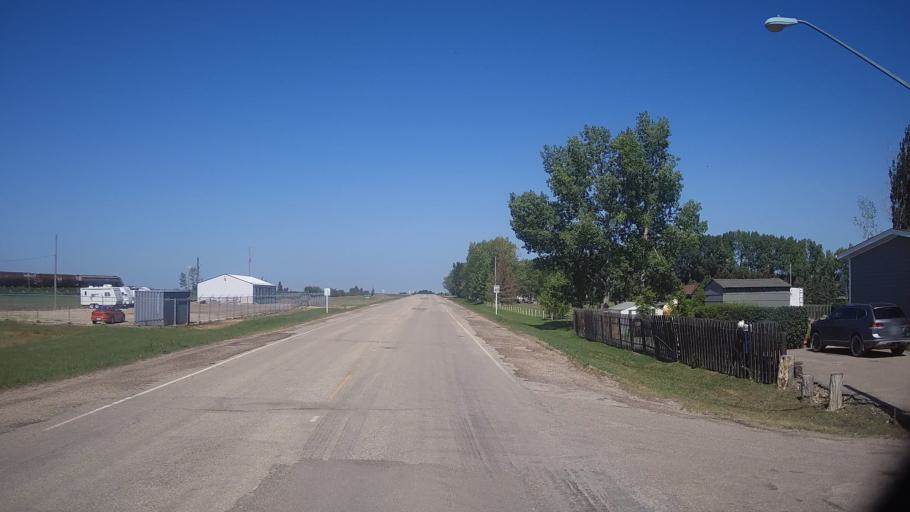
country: CA
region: Saskatchewan
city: Saskatoon
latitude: 51.8946
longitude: -106.0608
